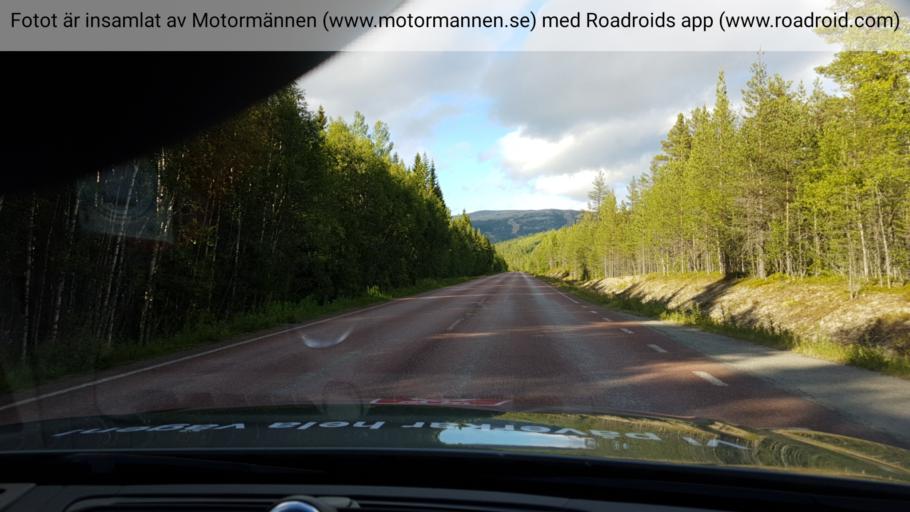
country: SE
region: Jaemtland
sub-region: Harjedalens Kommun
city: Sveg
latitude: 62.4697
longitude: 13.8785
